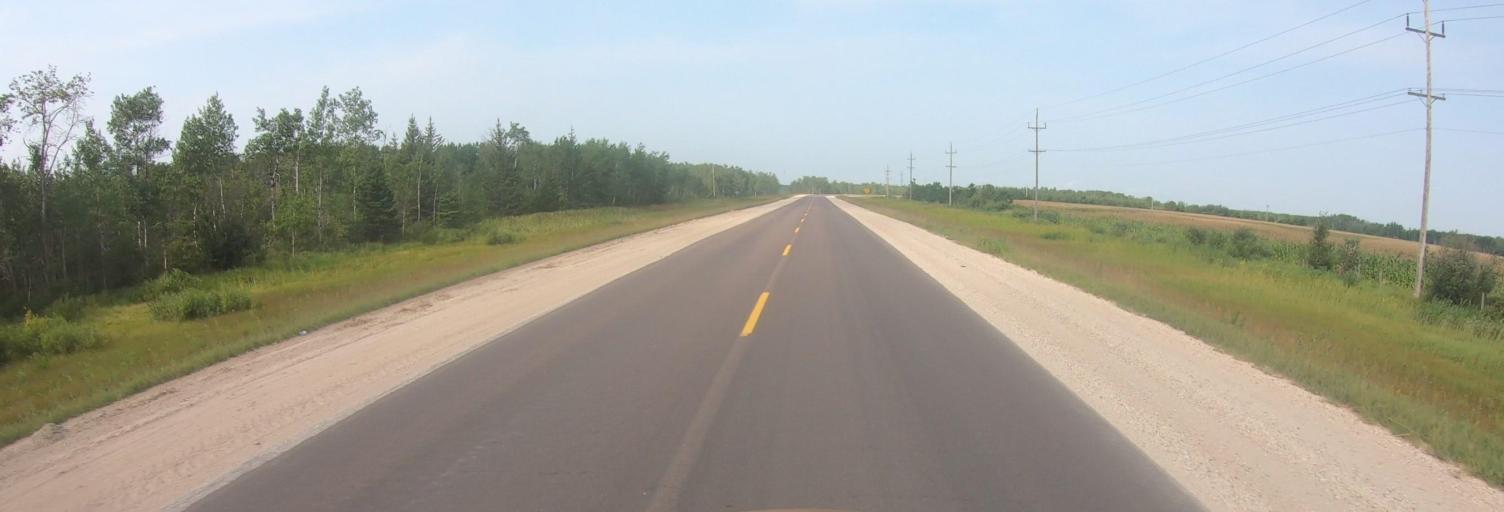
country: CA
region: Manitoba
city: La Broquerie
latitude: 49.2669
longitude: -96.4681
